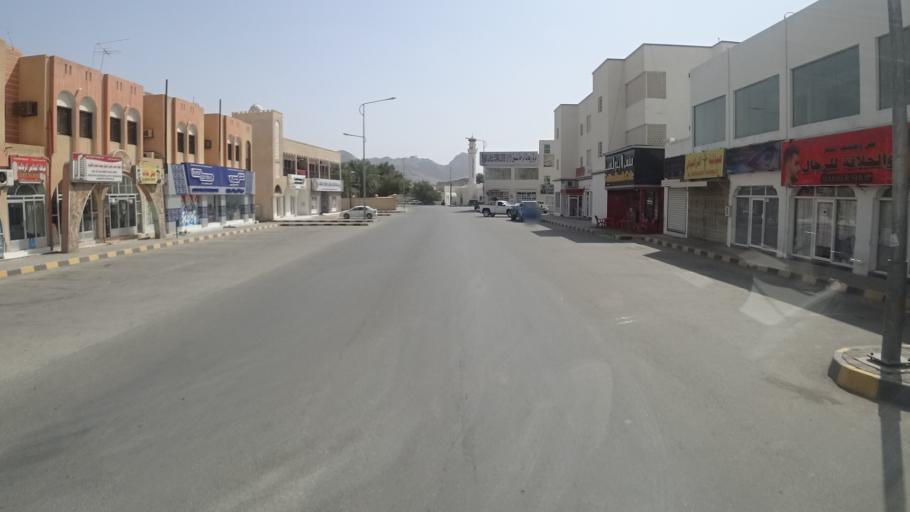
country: OM
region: Muhafazat ad Dakhiliyah
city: Bahla'
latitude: 23.1120
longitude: 57.2919
